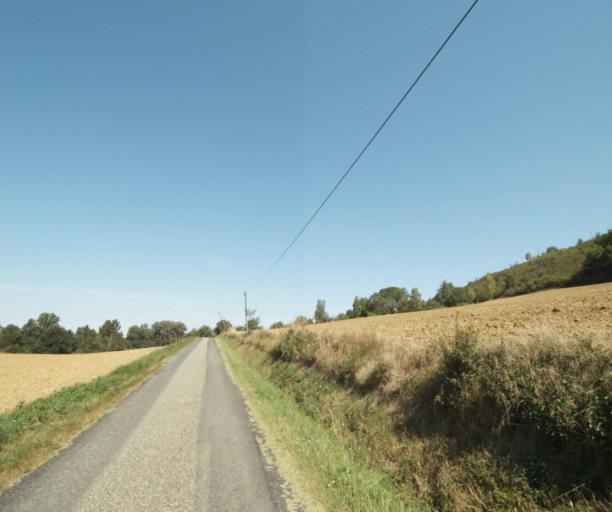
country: FR
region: Midi-Pyrenees
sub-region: Departement de l'Ariege
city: Lezat-sur-Leze
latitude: 43.2630
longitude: 1.3633
